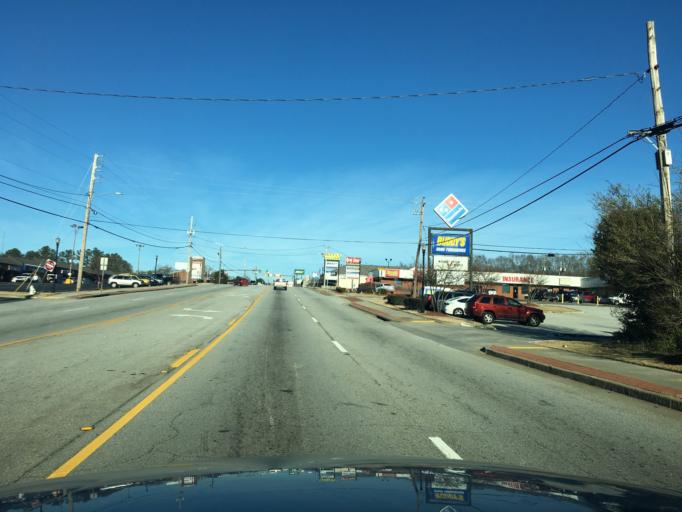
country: US
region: Georgia
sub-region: Rockdale County
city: Conyers
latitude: 33.6655
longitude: -84.0277
